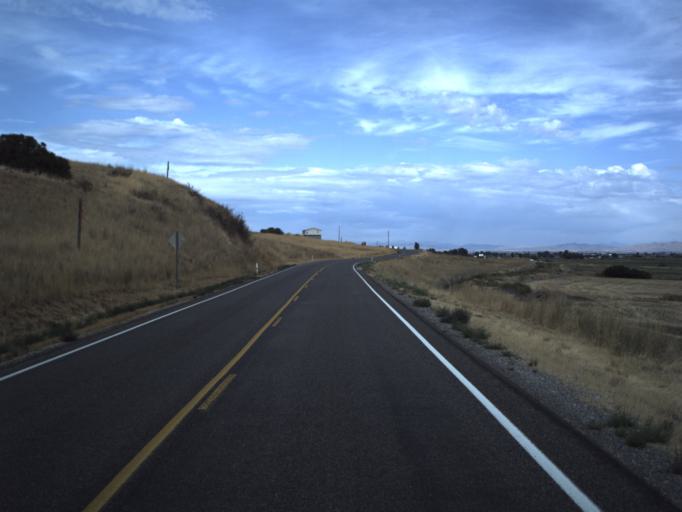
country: US
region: Utah
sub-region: Cache County
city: Benson
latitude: 41.8896
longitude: -111.9499
